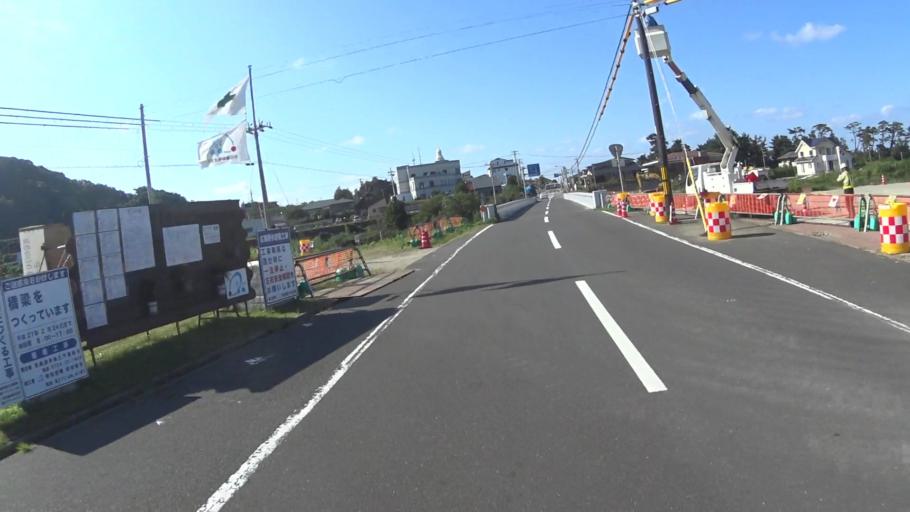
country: JP
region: Kyoto
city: Miyazu
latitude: 35.7386
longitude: 135.1042
